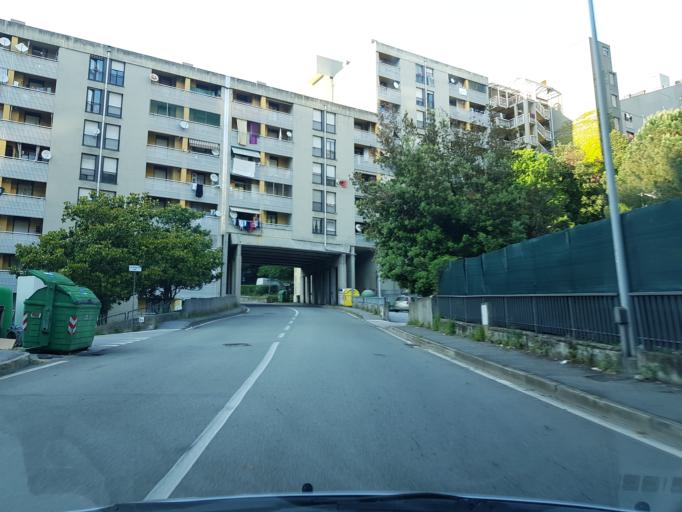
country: IT
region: Liguria
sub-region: Provincia di Genova
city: Genoa
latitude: 44.4519
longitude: 8.9068
